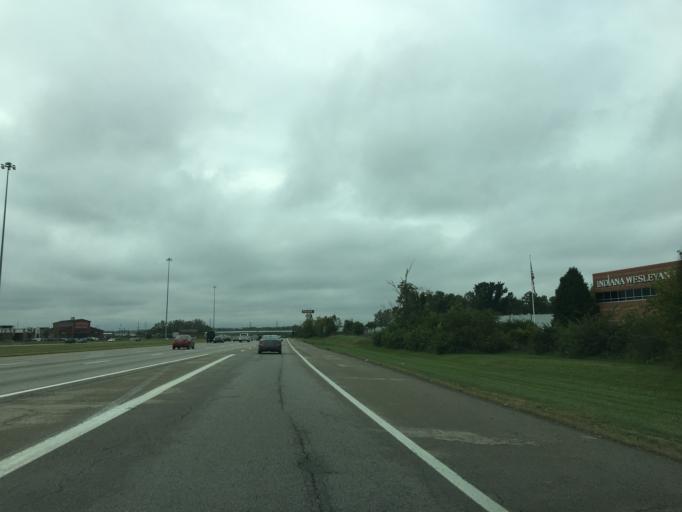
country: US
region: Ohio
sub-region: Butler County
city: Beckett Ridge
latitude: 39.3207
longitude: -84.4265
